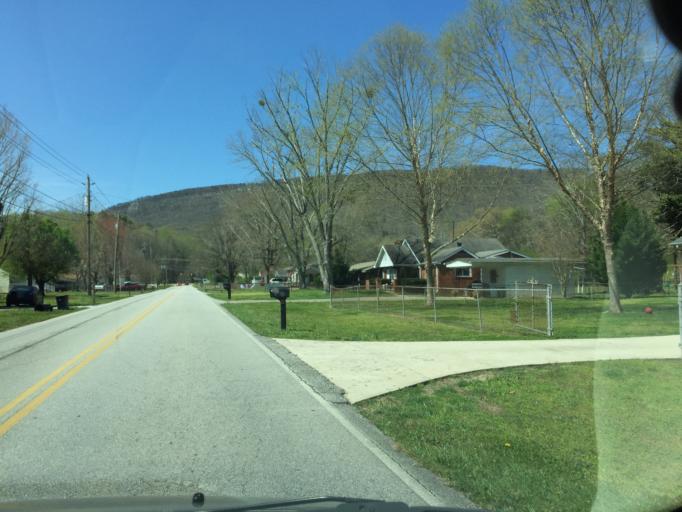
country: US
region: Tennessee
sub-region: Hamilton County
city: Falling Water
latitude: 35.2156
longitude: -85.2238
